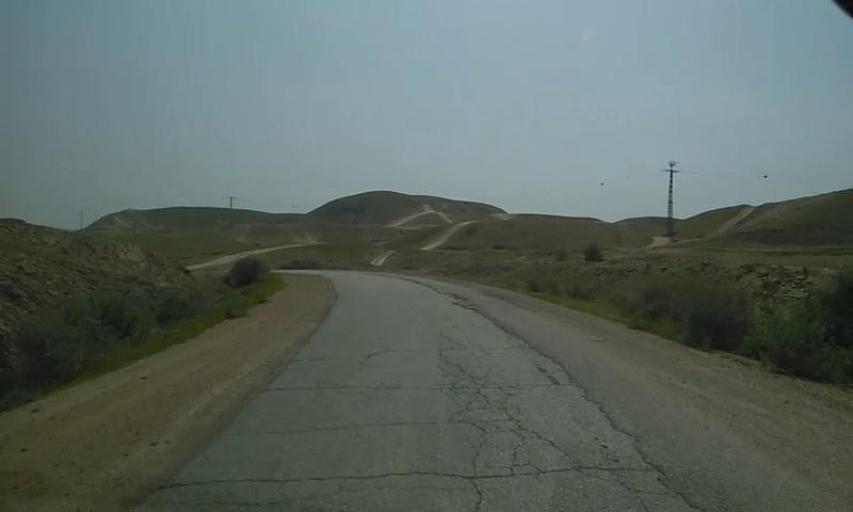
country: PS
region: West Bank
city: Jericho
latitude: 31.7962
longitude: 35.4267
